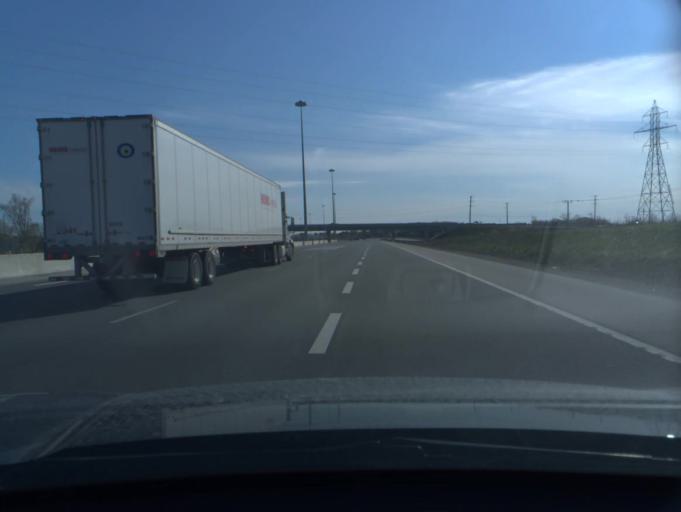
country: CA
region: Ontario
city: North Perth
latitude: 43.8082
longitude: -80.9999
